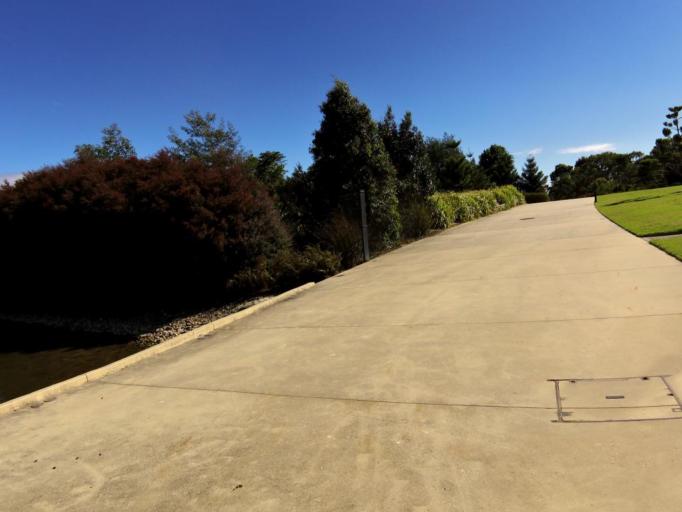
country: AU
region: Victoria
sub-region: Casey
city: Botanic Ridge
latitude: -38.1273
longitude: 145.2699
